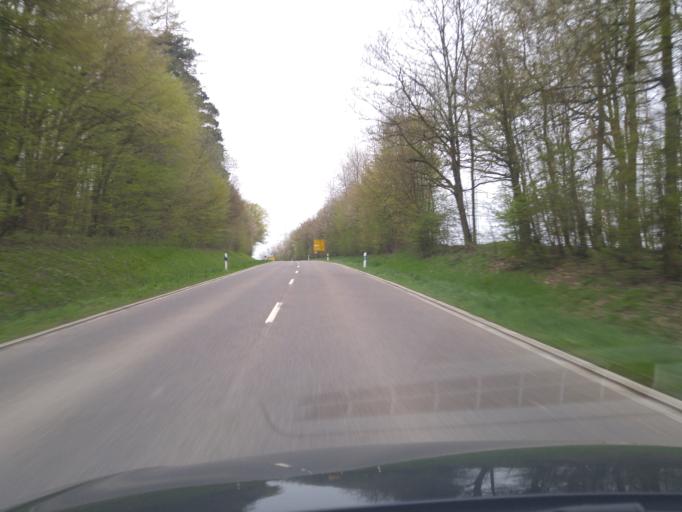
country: DE
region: Baden-Wuerttemberg
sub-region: Karlsruhe Region
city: Huffenhardt
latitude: 49.3238
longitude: 9.0704
